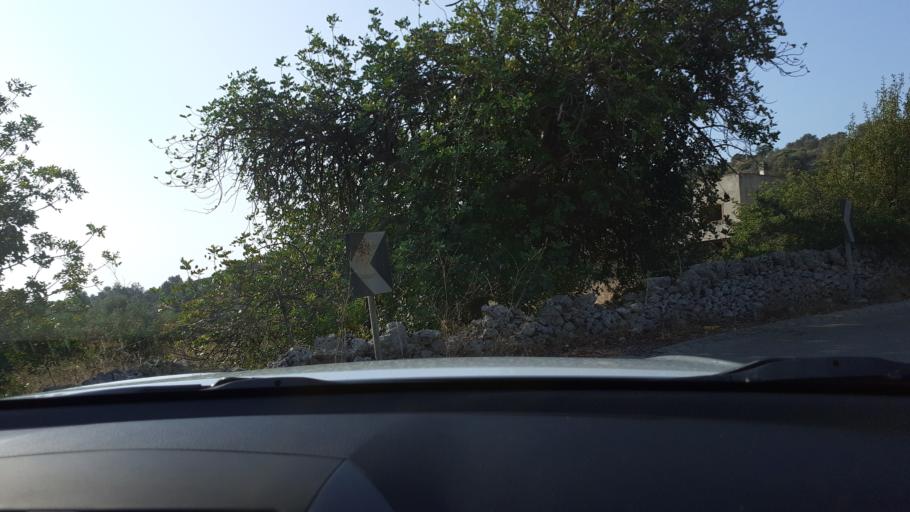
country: IT
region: Sicily
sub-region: Provincia di Siracusa
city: Cassibile
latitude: 36.9782
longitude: 15.1606
